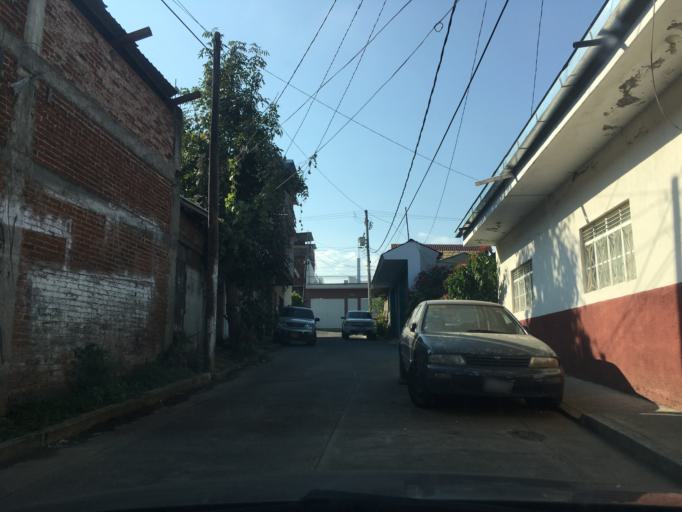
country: MX
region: Michoacan
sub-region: Uruapan
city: Uruapan
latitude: 19.4159
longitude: -102.0673
